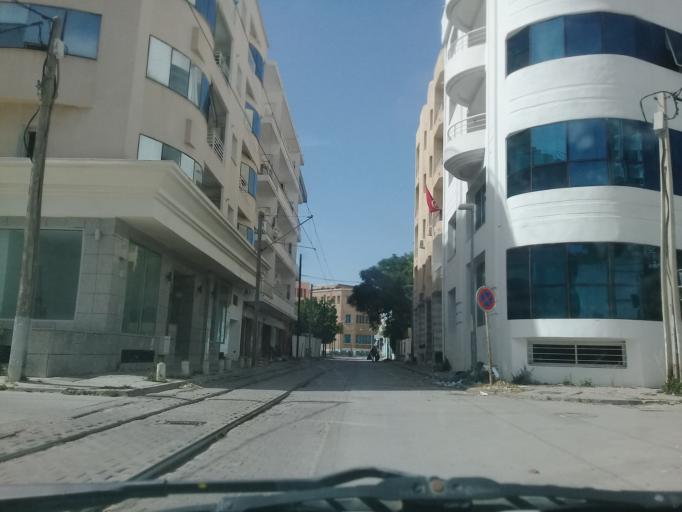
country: TN
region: Tunis
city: Tunis
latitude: 36.8180
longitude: 10.1815
